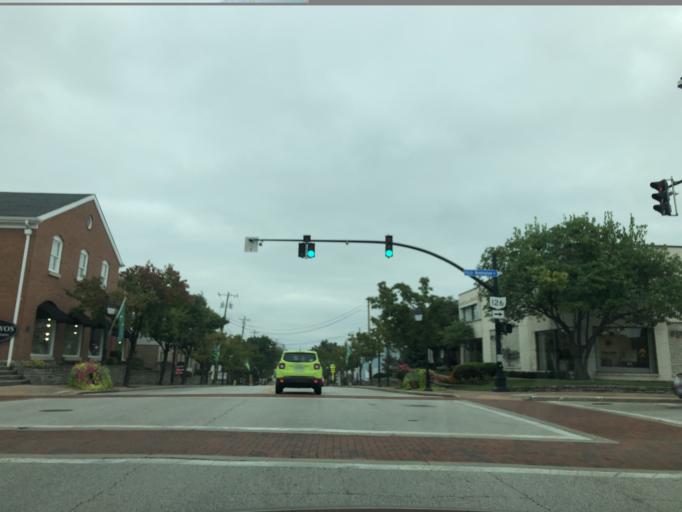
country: US
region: Ohio
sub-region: Hamilton County
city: Montgomery
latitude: 39.2279
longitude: -84.3542
